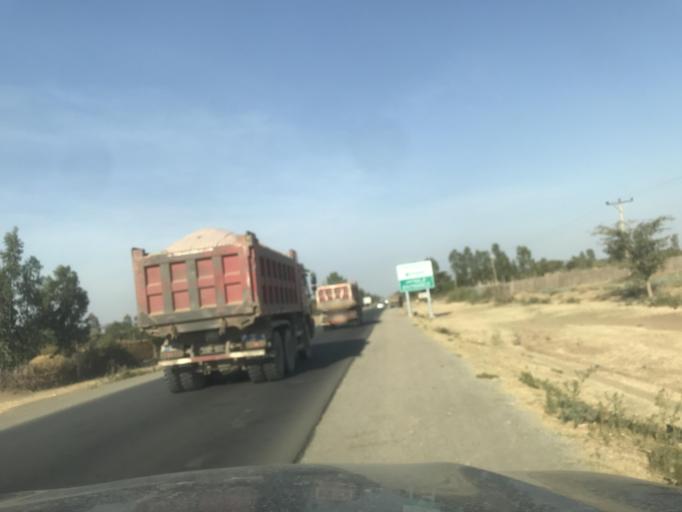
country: ET
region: Oromiya
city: Mojo
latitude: 8.2903
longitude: 38.9406
